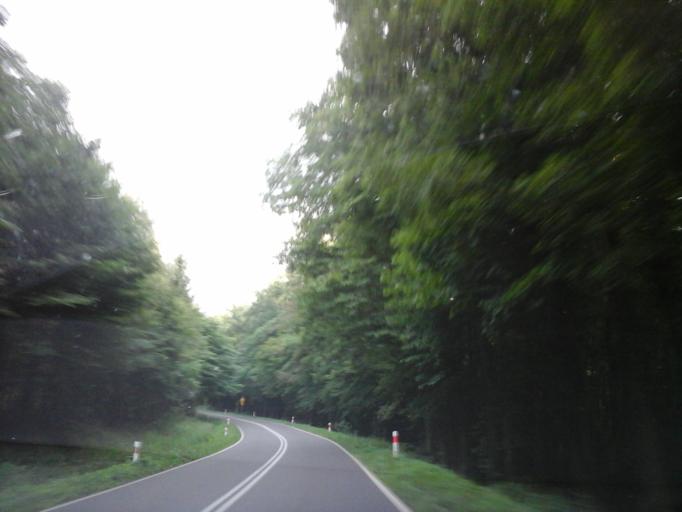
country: PL
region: West Pomeranian Voivodeship
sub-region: Powiat kamienski
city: Golczewo
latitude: 53.8374
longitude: 14.9574
